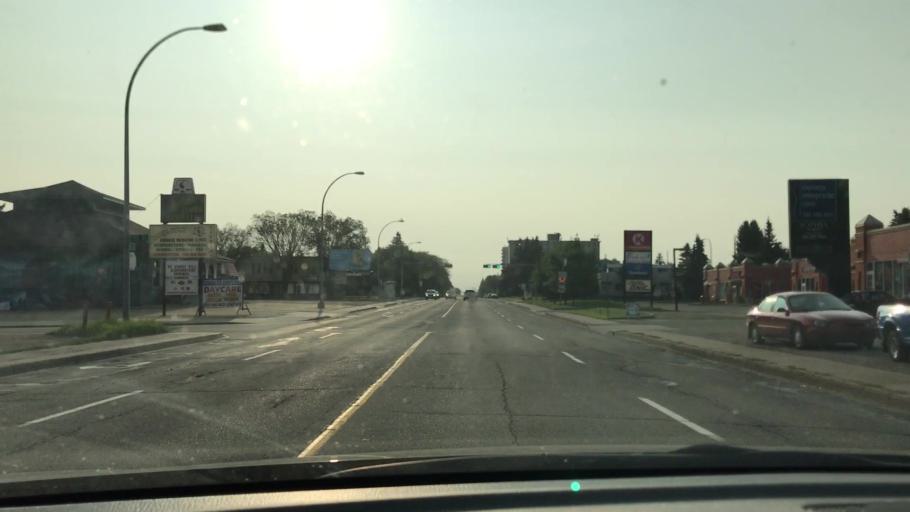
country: CA
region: Alberta
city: Edmonton
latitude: 53.5412
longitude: -113.4389
